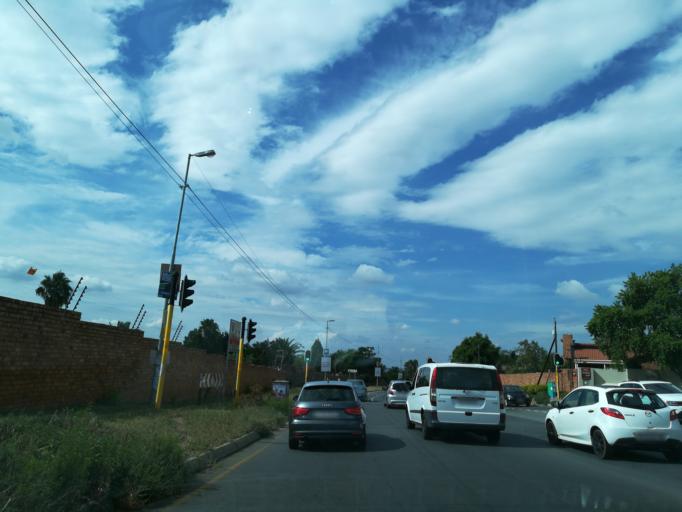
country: ZA
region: Gauteng
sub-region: West Rand District Municipality
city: Muldersdriseloop
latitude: -26.0588
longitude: 27.9578
